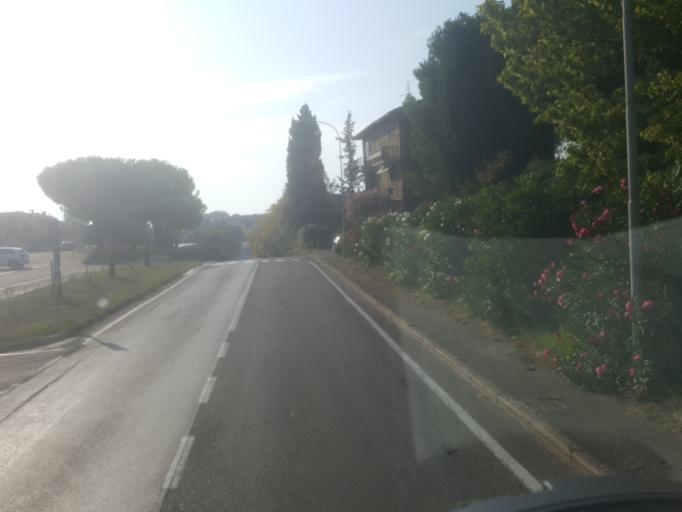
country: IT
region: Tuscany
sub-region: Province of Florence
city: Montaione
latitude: 43.5471
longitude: 10.9231
